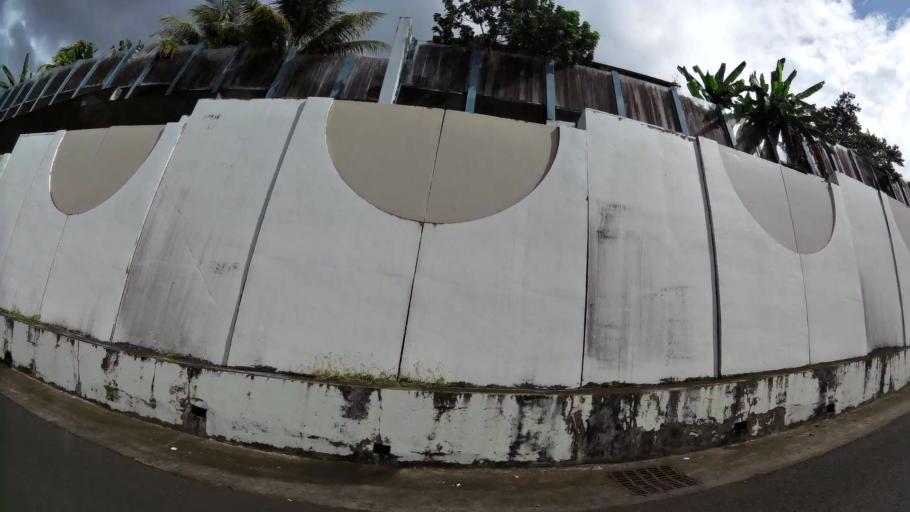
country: MQ
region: Martinique
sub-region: Martinique
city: Ducos
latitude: 14.5737
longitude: -60.9845
